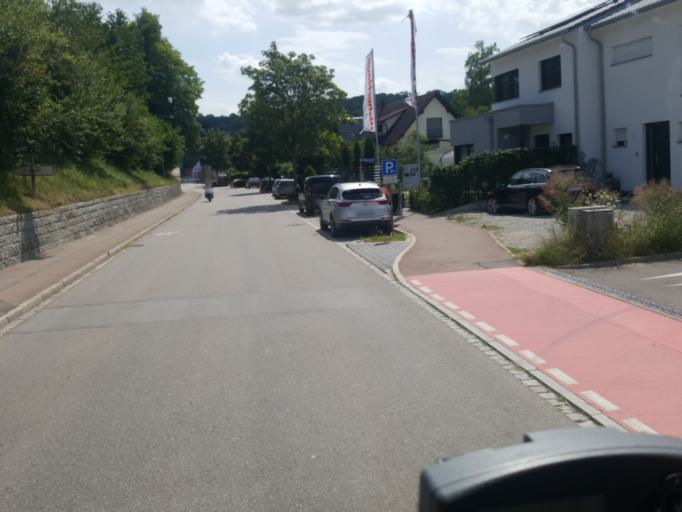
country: DE
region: Baden-Wuerttemberg
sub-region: Freiburg Region
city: Schliengen
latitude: 47.7583
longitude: 7.5774
